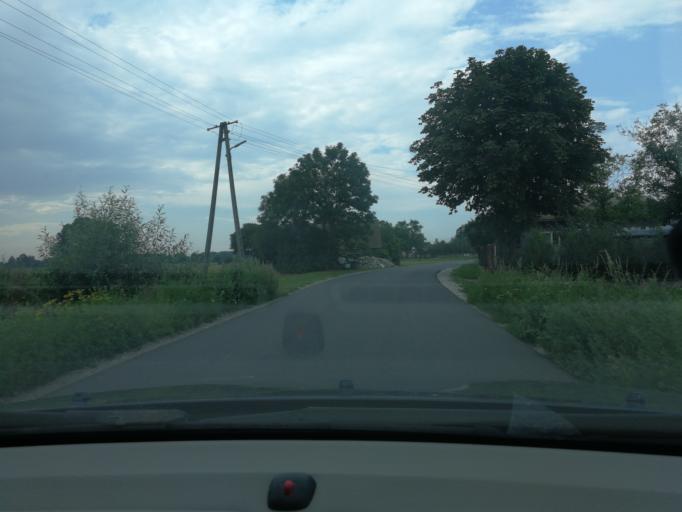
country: PL
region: Masovian Voivodeship
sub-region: Powiat warszawski zachodni
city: Bieniewice
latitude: 52.1056
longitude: 20.5551
